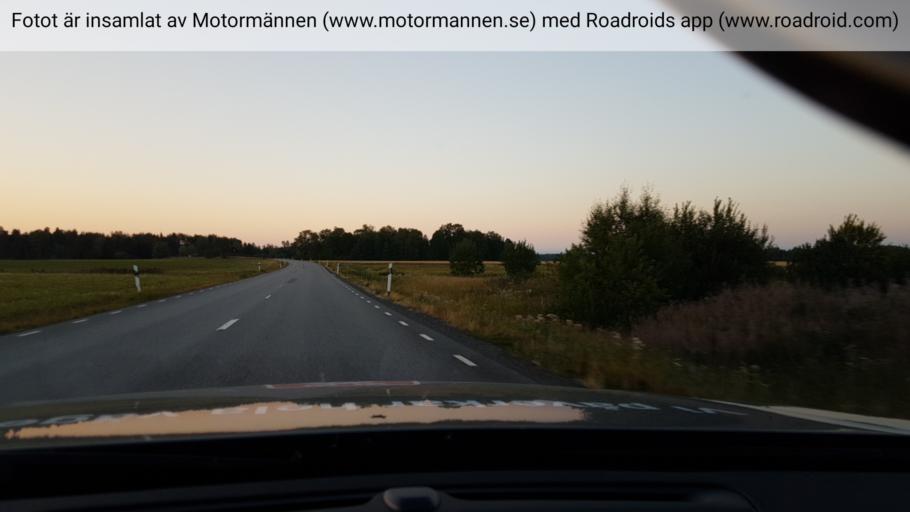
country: SE
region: Uppsala
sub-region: Heby Kommun
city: OEstervala
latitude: 60.1155
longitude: 17.2165
